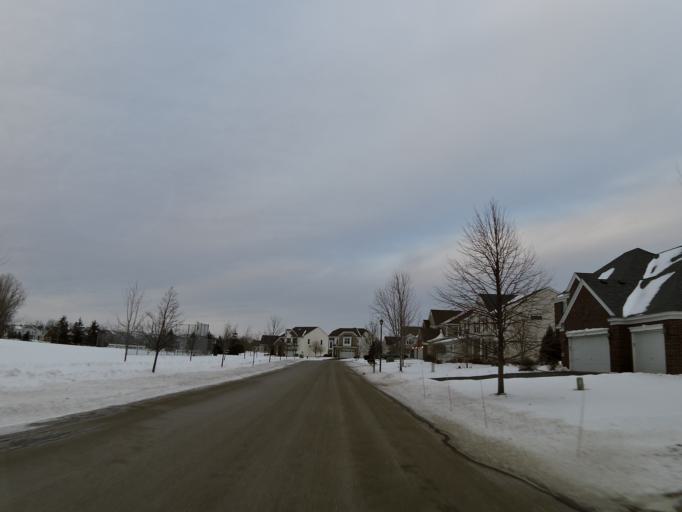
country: US
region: Minnesota
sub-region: Washington County
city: Woodbury
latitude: 44.9139
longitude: -92.8875
